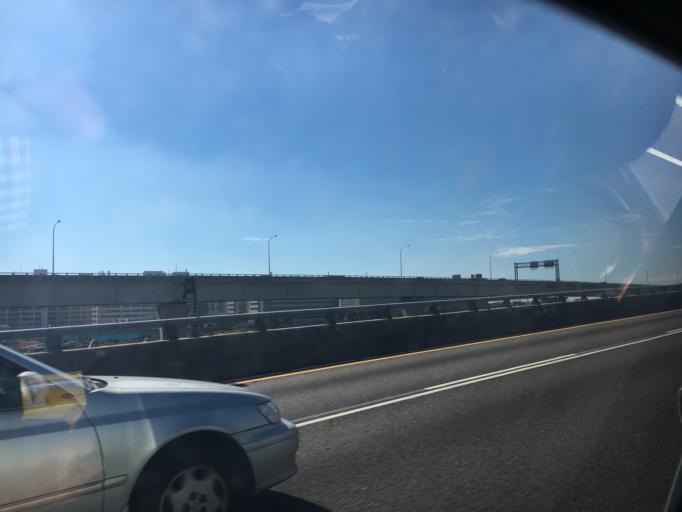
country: TW
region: Taiwan
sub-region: Taoyuan
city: Taoyuan
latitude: 25.0660
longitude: 121.3702
